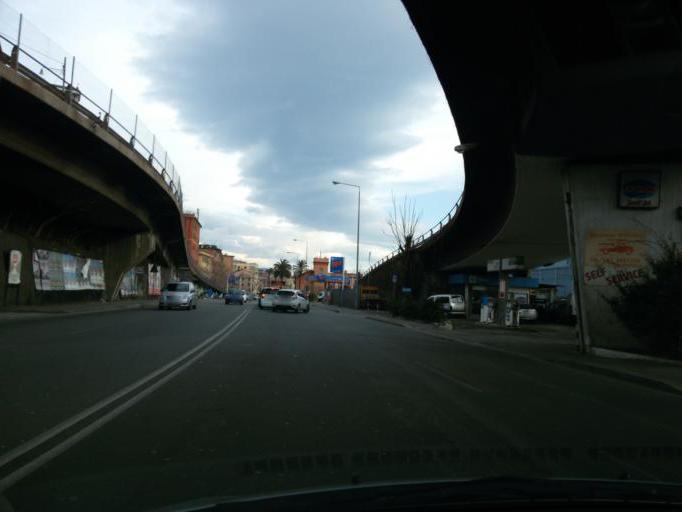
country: IT
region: Liguria
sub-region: Provincia di Genova
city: San Teodoro
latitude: 44.4155
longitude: 8.8618
